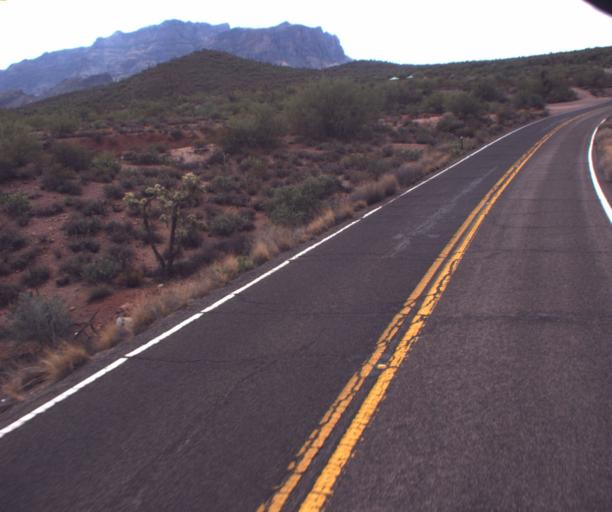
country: US
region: Arizona
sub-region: Pinal County
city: Apache Junction
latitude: 33.4983
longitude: -111.4632
